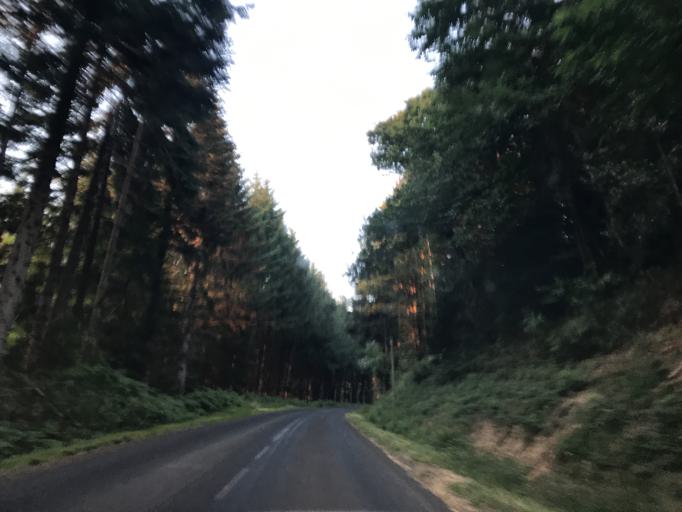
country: FR
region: Auvergne
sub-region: Departement du Puy-de-Dome
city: Celles-sur-Durolle
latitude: 45.7551
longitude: 3.6608
